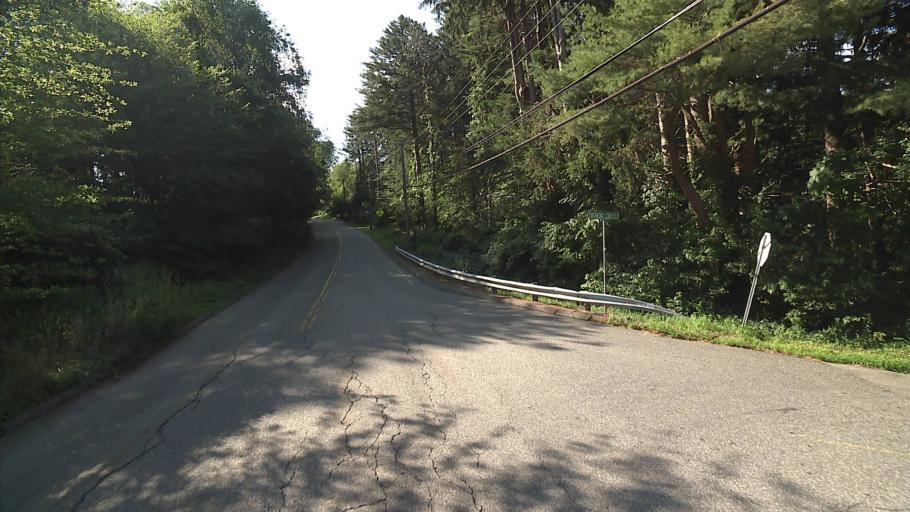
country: US
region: Connecticut
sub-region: New London County
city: Montville Center
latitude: 41.4972
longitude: -72.1968
